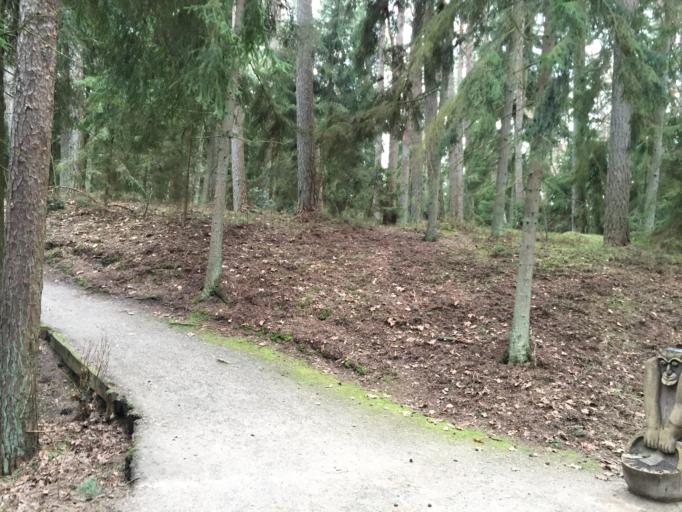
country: LT
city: Neringa
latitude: 55.5381
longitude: 21.1095
